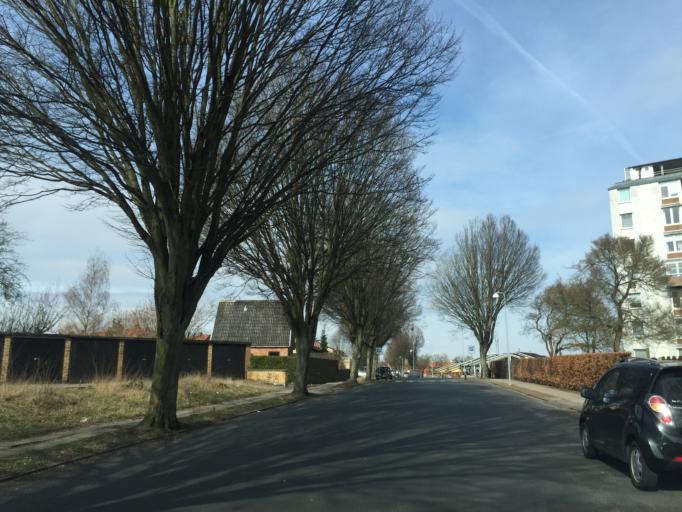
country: DK
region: South Denmark
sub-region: Odense Kommune
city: Neder Holluf
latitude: 55.3936
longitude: 10.4303
